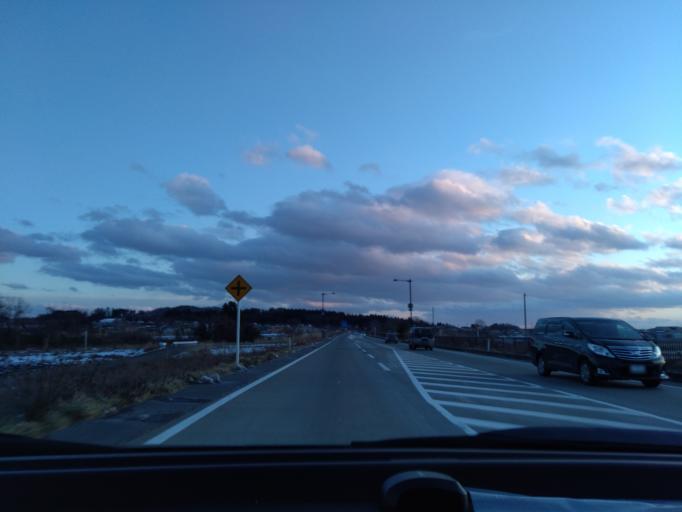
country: JP
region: Iwate
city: Hanamaki
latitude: 39.3938
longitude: 141.1427
